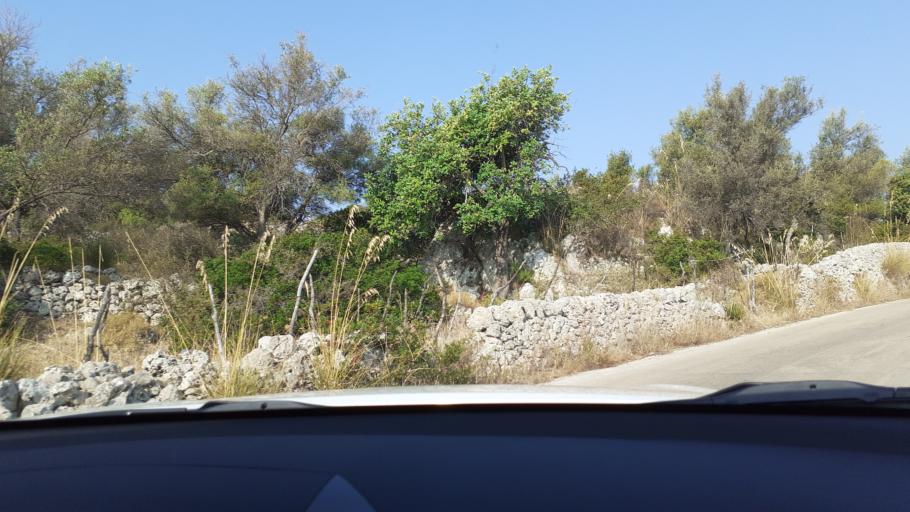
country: IT
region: Sicily
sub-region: Provincia di Siracusa
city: Cassibile
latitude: 36.9770
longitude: 15.1602
